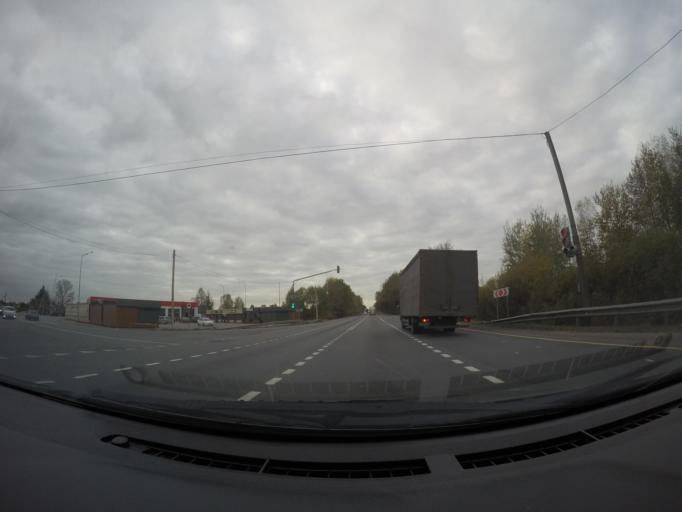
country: RU
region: Moskovskaya
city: Gzhel'
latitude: 55.6452
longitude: 38.3718
